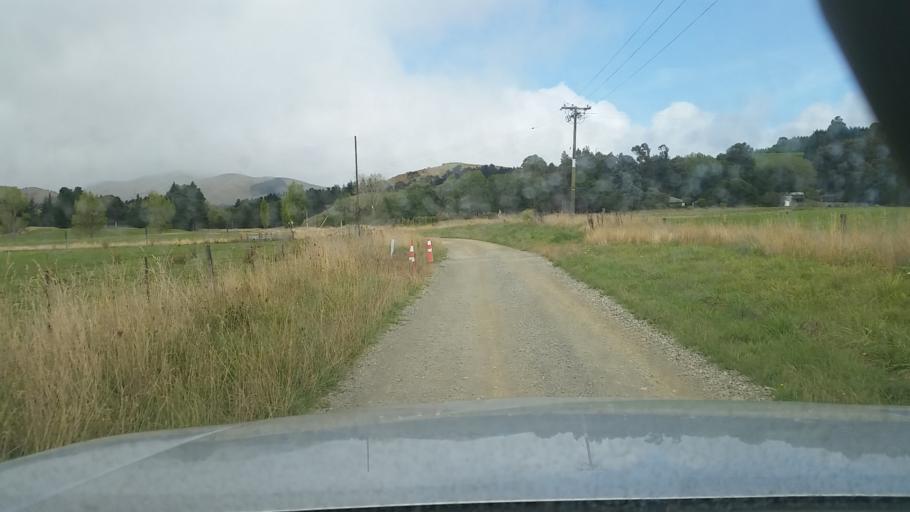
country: NZ
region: Marlborough
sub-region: Marlborough District
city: Blenheim
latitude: -41.7277
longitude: 173.9235
